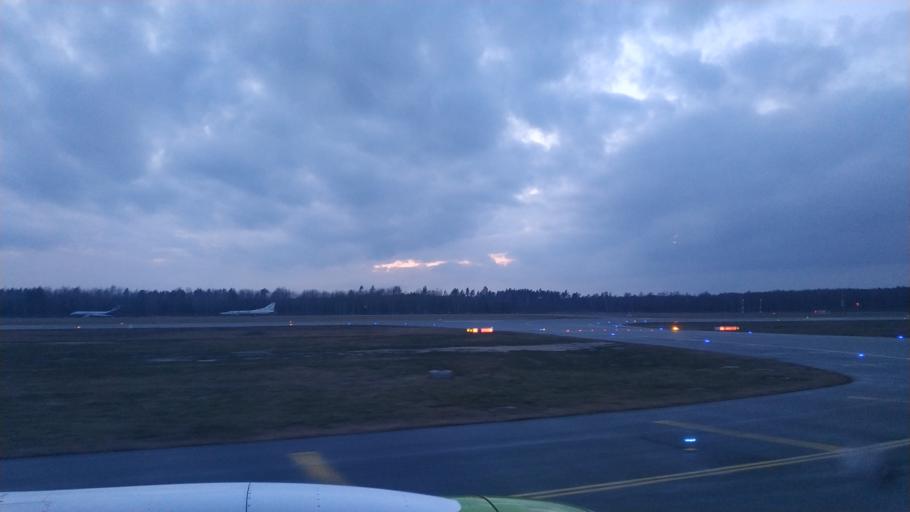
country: LV
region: Babite
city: Pinki
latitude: 56.9289
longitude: 23.9760
